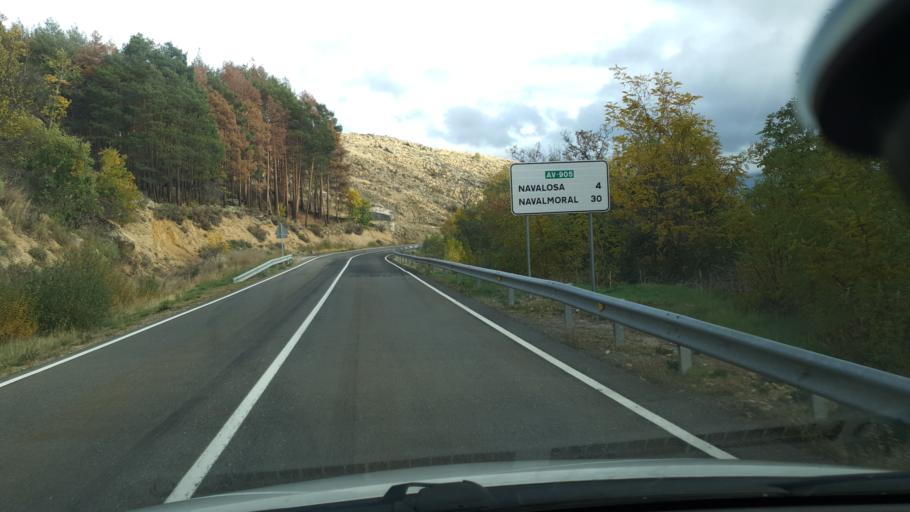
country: ES
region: Castille and Leon
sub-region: Provincia de Avila
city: Hoyocasero
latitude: 40.3978
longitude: -4.9665
